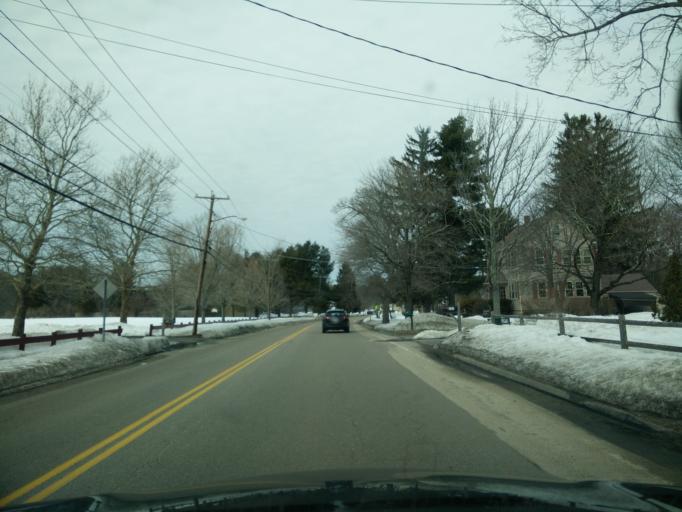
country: US
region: Massachusetts
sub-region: Norfolk County
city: Walpole
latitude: 42.1667
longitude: -71.2376
